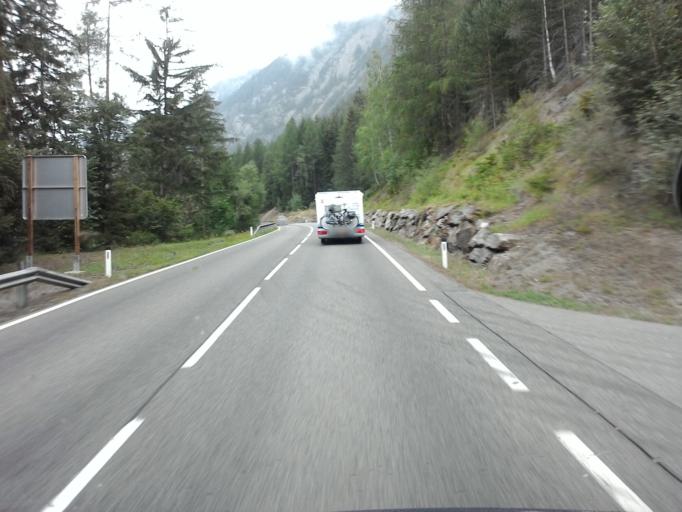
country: AT
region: Tyrol
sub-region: Politischer Bezirk Lienz
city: Matrei in Osttirol
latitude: 47.0118
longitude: 12.5395
